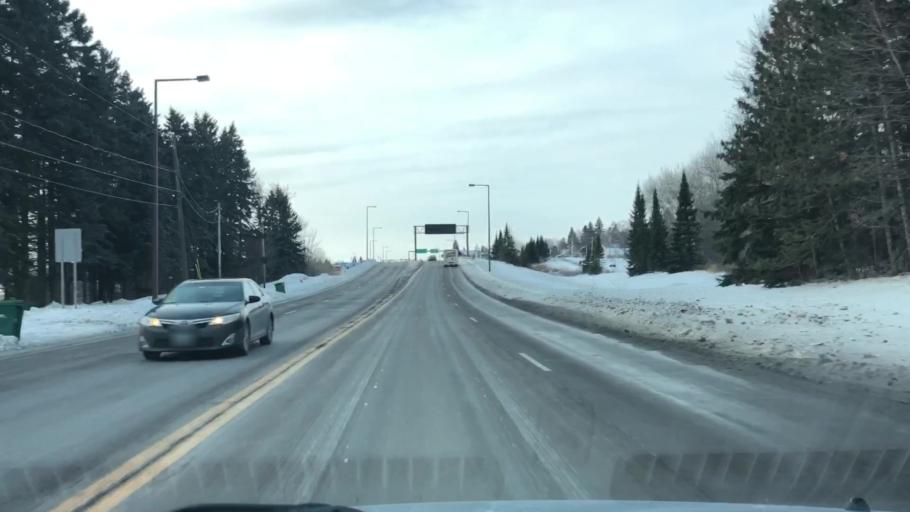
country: US
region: Minnesota
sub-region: Saint Louis County
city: Duluth
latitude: 46.8119
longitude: -92.0577
